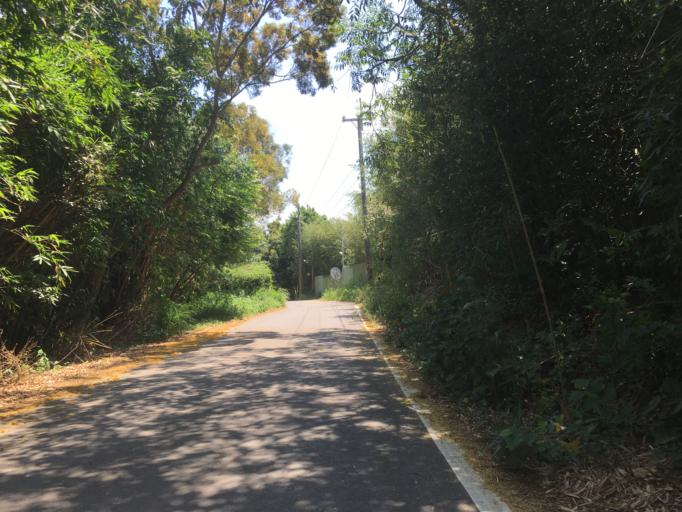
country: TW
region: Taiwan
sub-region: Hsinchu
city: Hsinchu
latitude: 24.7368
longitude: 120.9869
